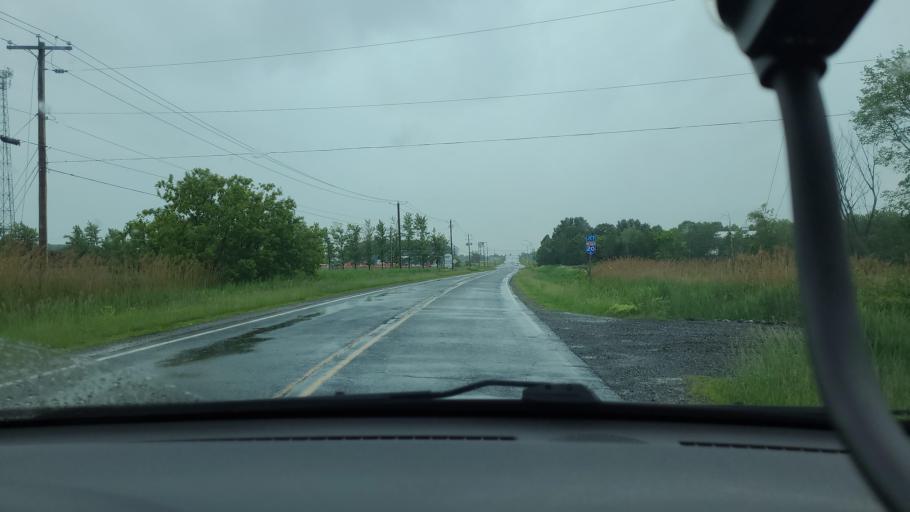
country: CA
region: Quebec
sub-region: Monteregie
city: Beloeil
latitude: 45.6133
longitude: -73.0989
